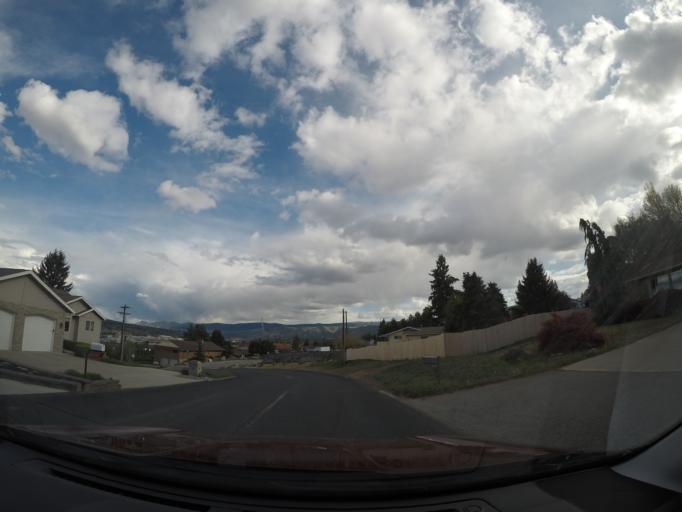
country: US
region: Washington
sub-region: Chelan County
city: West Wenatchee
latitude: 47.4556
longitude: -120.3420
